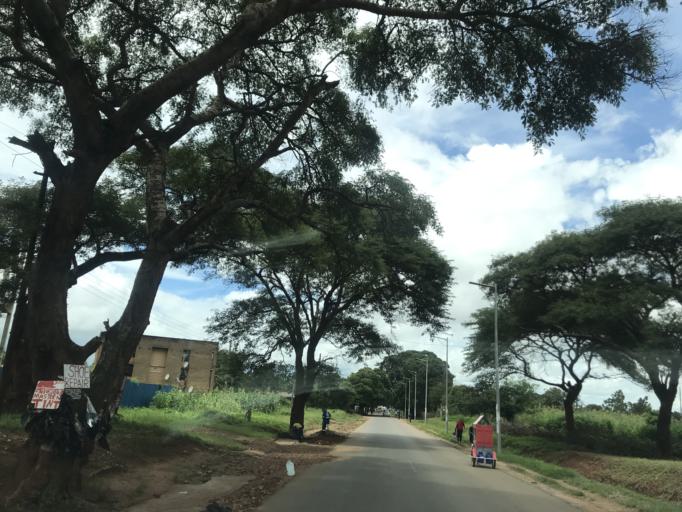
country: ZM
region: Lusaka
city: Lusaka
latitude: -15.4276
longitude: 28.3077
